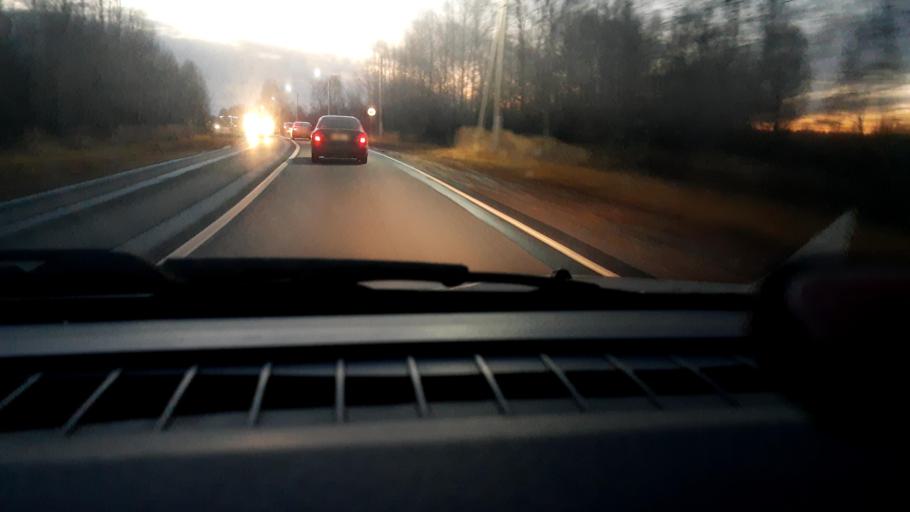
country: RU
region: Nizjnij Novgorod
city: Vladimirskoye
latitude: 56.8713
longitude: 44.9426
